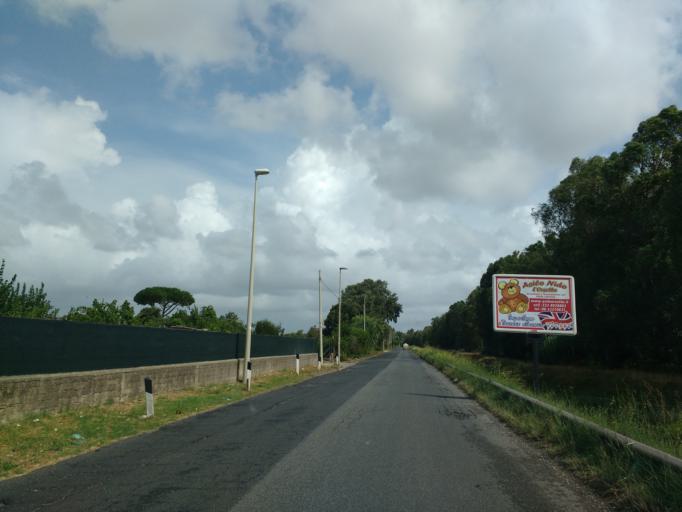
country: IT
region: Latium
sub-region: Citta metropolitana di Roma Capitale
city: Acilia-Castel Fusano-Ostia Antica
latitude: 41.7542
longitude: 12.3300
